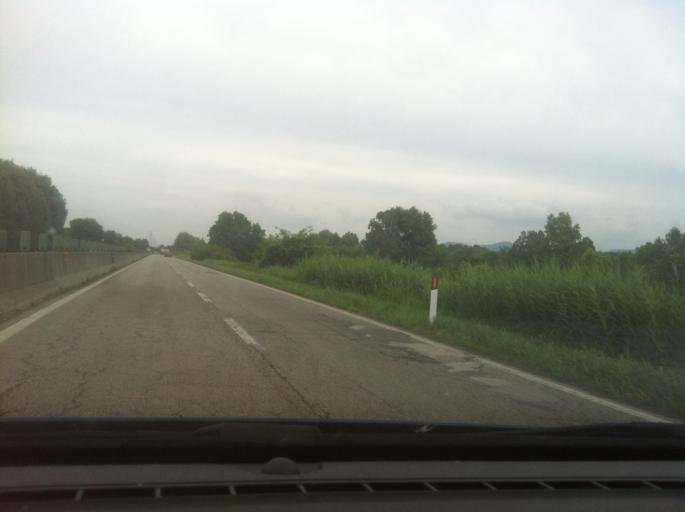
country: IT
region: Piedmont
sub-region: Provincia di Torino
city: Settimo Torinese
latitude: 45.1261
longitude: 7.7703
